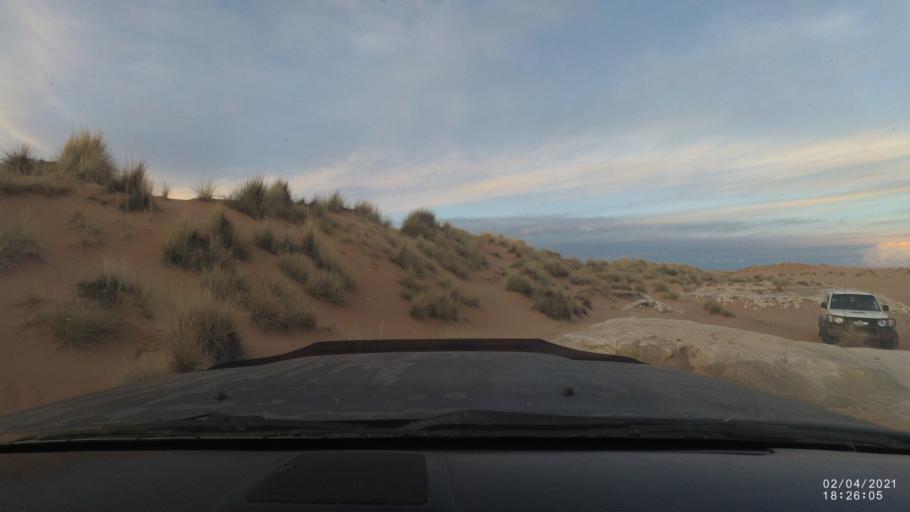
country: BO
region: Oruro
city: Poopo
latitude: -18.7050
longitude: -67.5328
